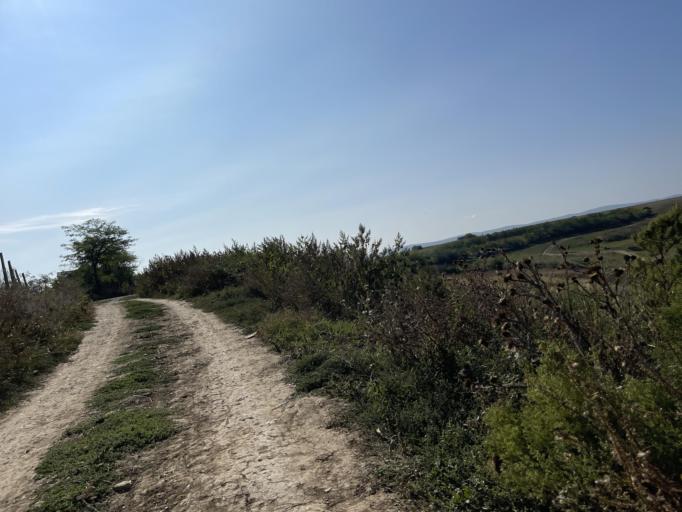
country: RO
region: Iasi
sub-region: Comuna Dumesti
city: Pausesti
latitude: 47.1527
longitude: 27.3162
